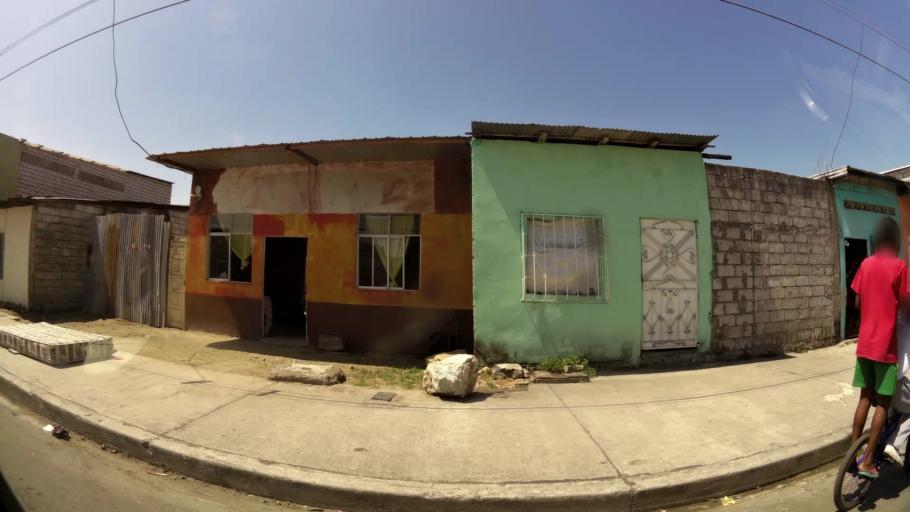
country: EC
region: Guayas
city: Guayaquil
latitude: -2.2329
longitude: -79.9197
